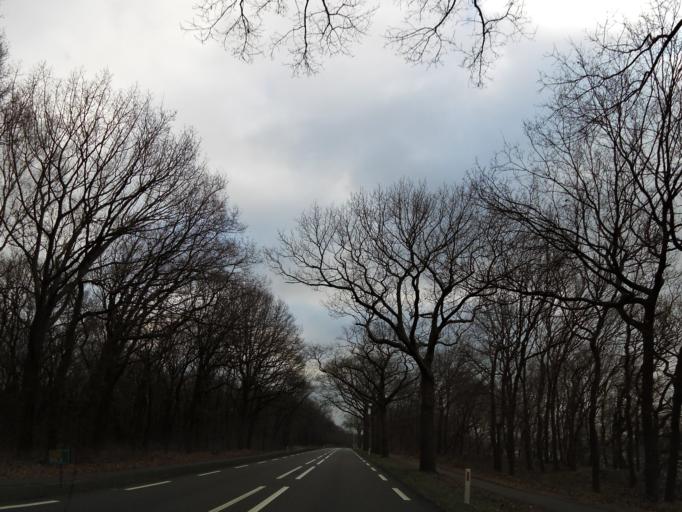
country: NL
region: Limburg
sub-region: Gemeente Bergen
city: Wellerlooi
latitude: 51.5112
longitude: 6.1655
